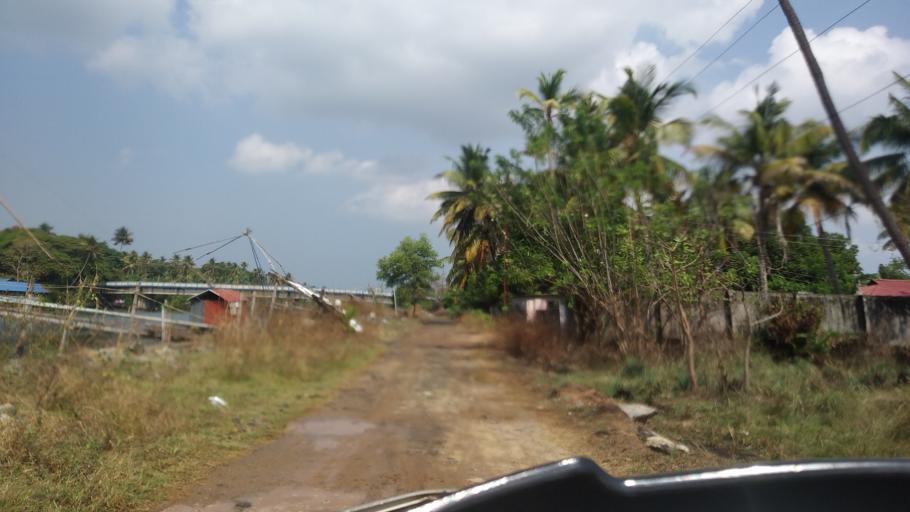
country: IN
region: Kerala
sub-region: Thrissur District
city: Kodungallur
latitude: 10.1389
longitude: 76.2036
